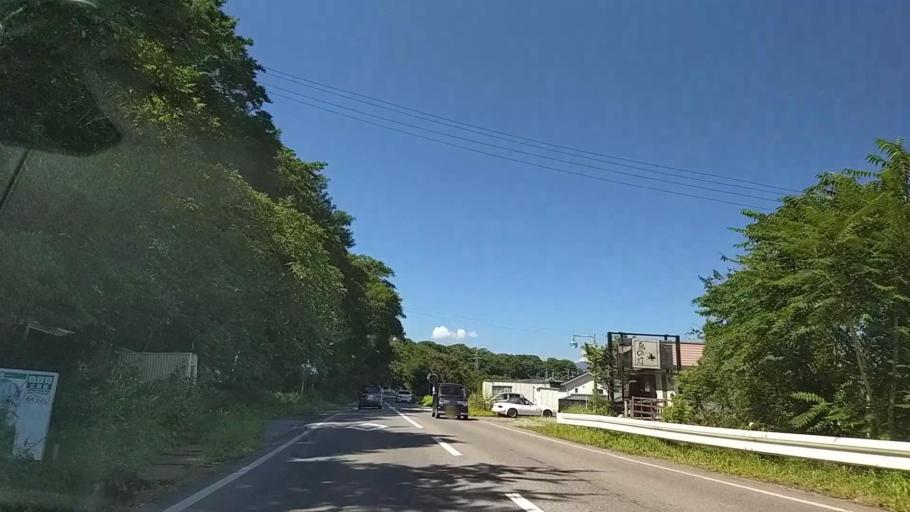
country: JP
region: Nagano
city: Kamimaruko
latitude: 36.3528
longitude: 138.3229
